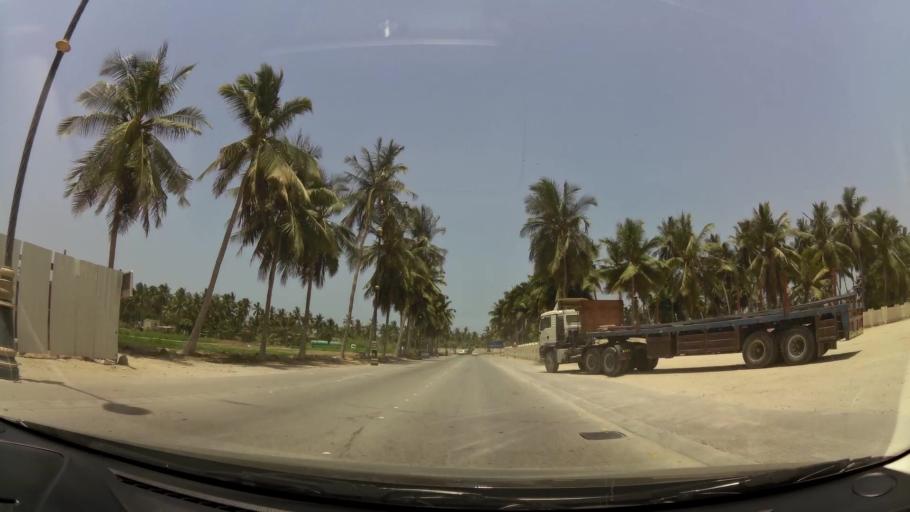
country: OM
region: Zufar
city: Salalah
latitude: 17.0128
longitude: 54.1097
